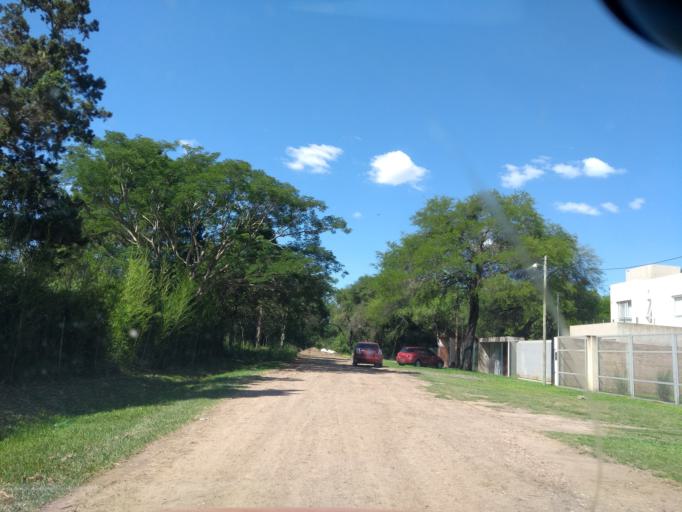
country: AR
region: Chaco
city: Resistencia
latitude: -27.4216
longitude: -58.9449
